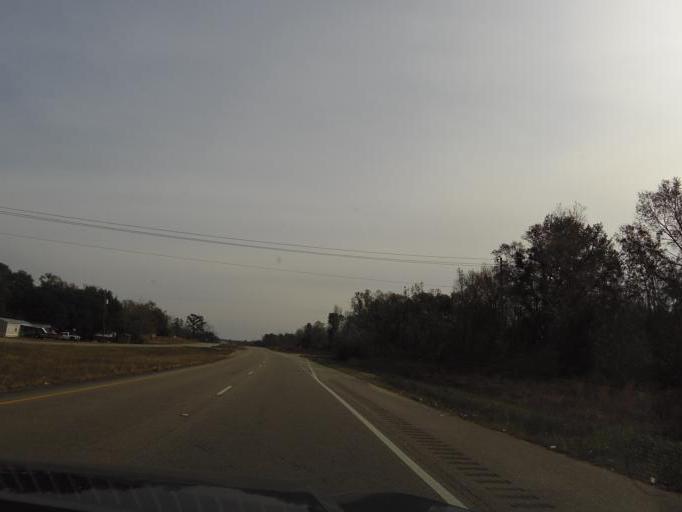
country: US
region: Alabama
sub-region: Houston County
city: Ashford
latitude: 31.1609
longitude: -85.1904
